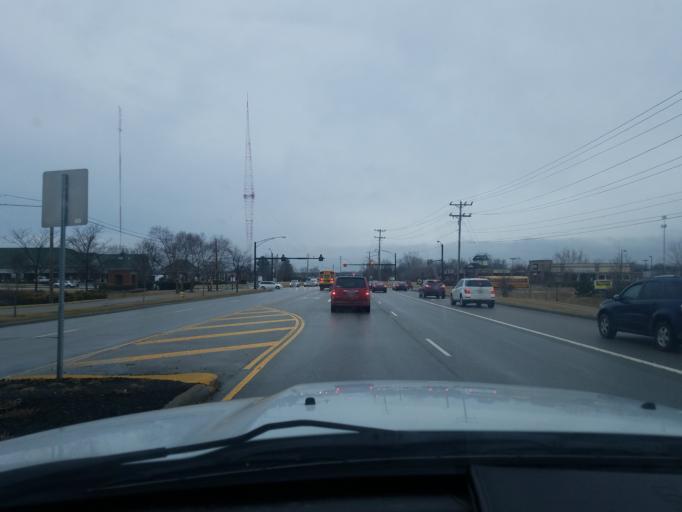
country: US
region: Ohio
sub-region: Warren County
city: Mason
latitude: 39.3520
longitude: -84.3325
